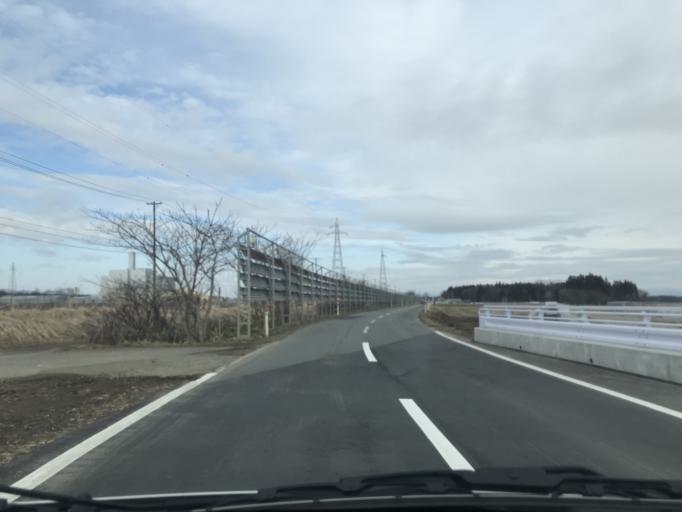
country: JP
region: Iwate
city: Kitakami
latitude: 39.3227
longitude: 141.0132
